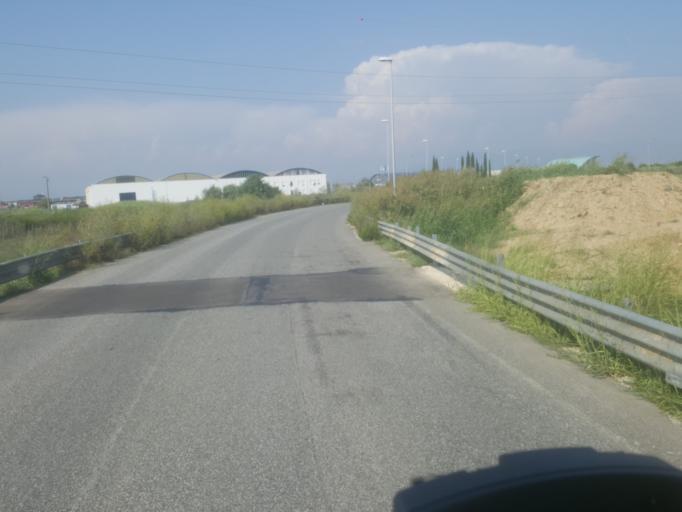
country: IT
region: Tuscany
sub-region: Provincia di Livorno
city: Guasticce
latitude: 43.5996
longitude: 10.4009
